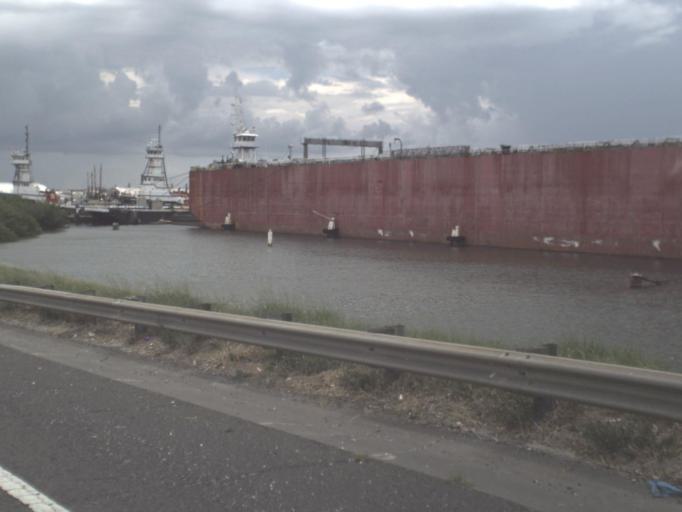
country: US
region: Florida
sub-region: Hillsborough County
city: Tampa
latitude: 27.9316
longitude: -82.4290
